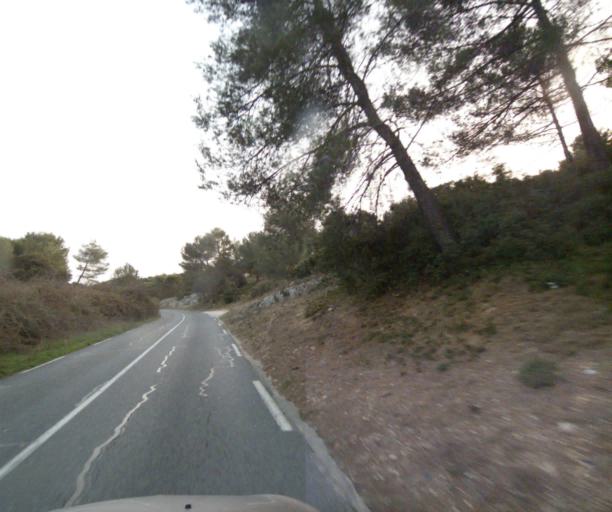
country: FR
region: Provence-Alpes-Cote d'Azur
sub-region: Departement des Bouches-du-Rhone
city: Cabries
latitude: 43.4302
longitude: 5.3673
